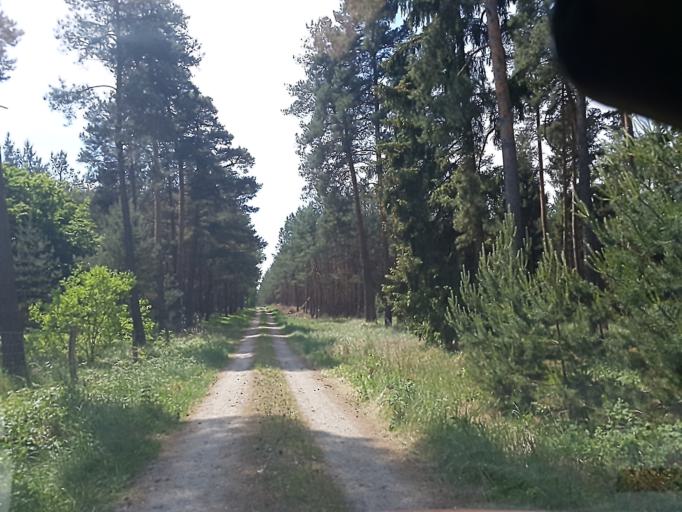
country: DE
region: Brandenburg
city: Gorzke
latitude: 52.1108
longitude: 12.2991
